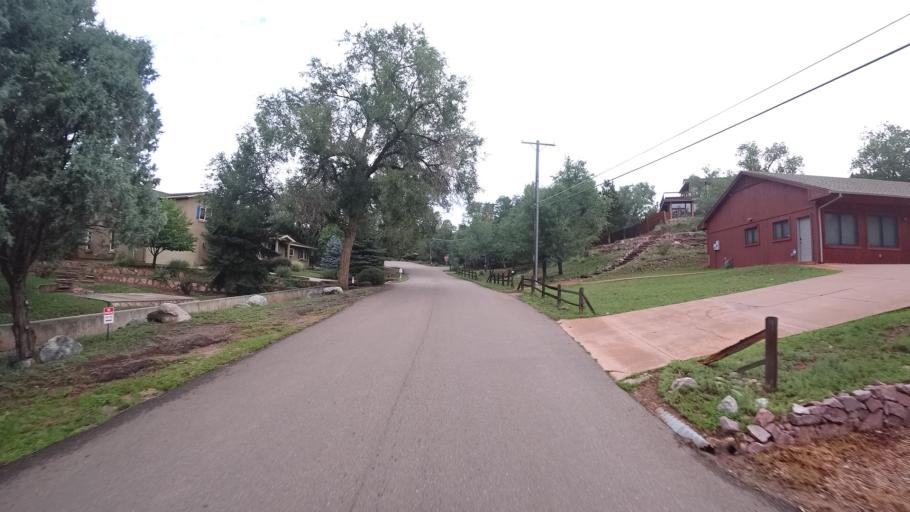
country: US
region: Colorado
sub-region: El Paso County
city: Manitou Springs
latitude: 38.8596
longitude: -104.8882
